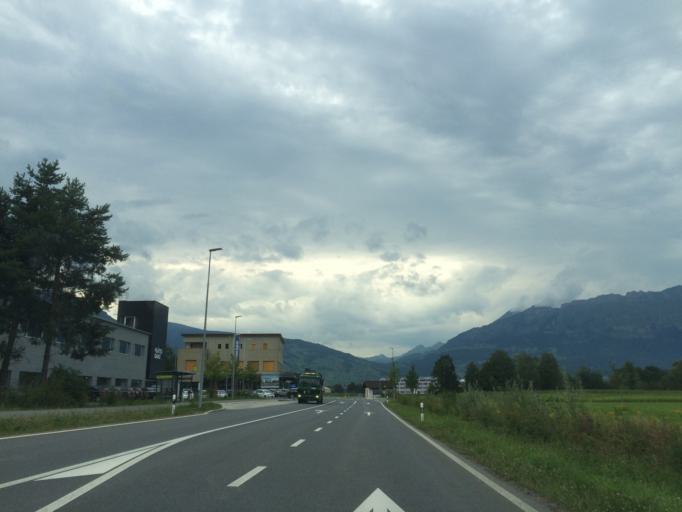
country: LI
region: Schaan
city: Schaan
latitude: 47.1778
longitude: 9.5139
